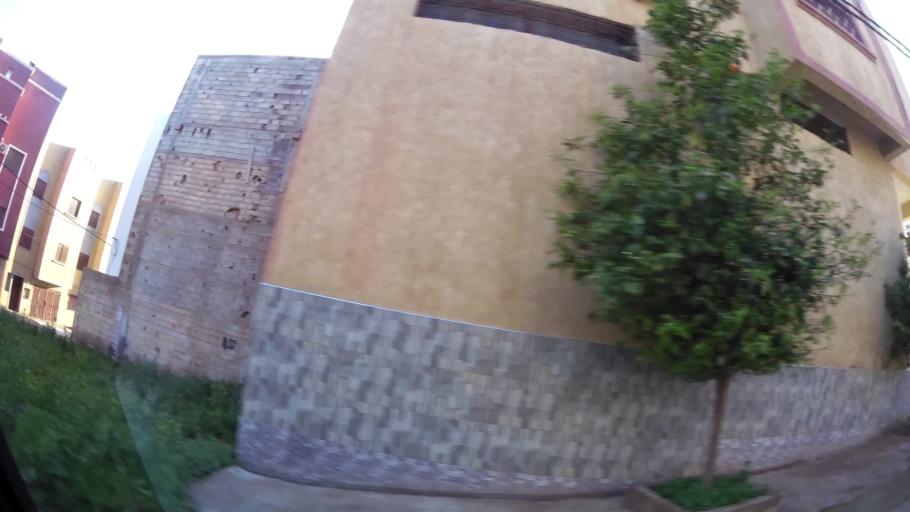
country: MA
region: Chaouia-Ouardigha
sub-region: Settat Province
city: Settat
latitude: 33.0029
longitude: -7.6025
